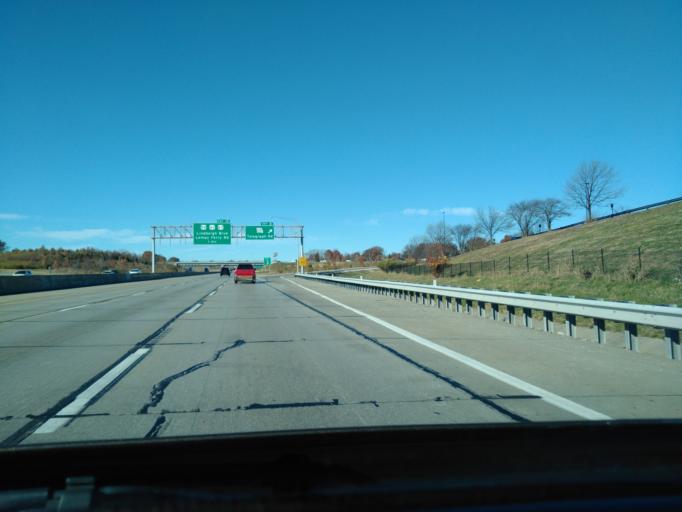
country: US
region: Missouri
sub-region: Saint Louis County
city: Oakville
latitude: 38.4931
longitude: -90.2967
